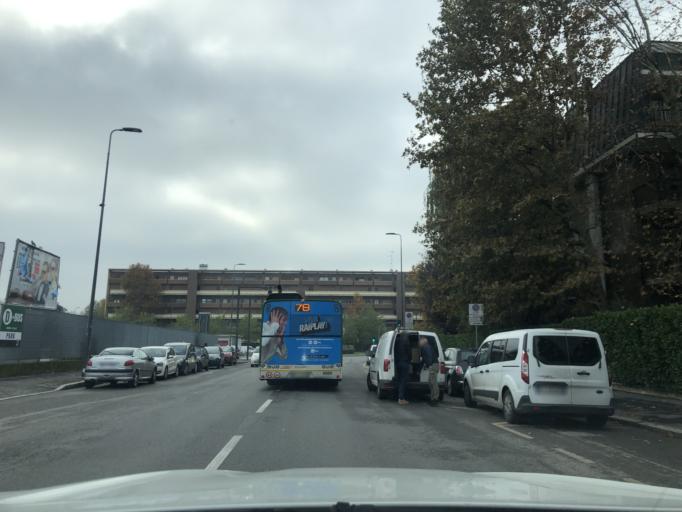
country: IT
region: Lombardy
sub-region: Citta metropolitana di Milano
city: Romano Banco
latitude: 45.4772
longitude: 9.1175
